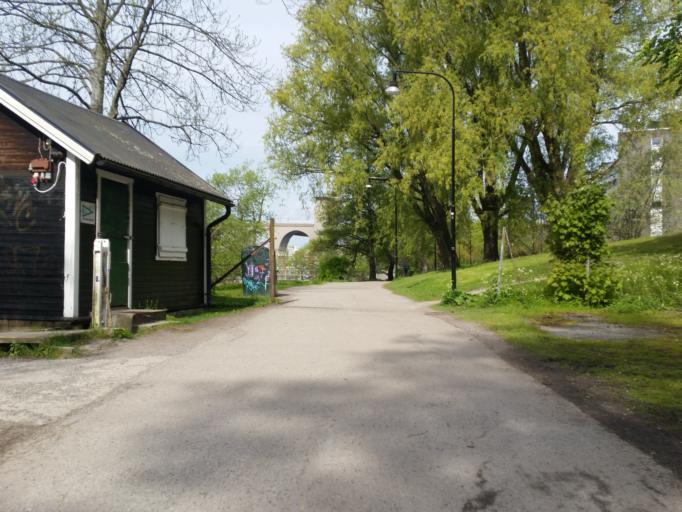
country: SE
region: Stockholm
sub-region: Stockholms Kommun
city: Arsta
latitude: 59.3086
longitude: 18.0502
